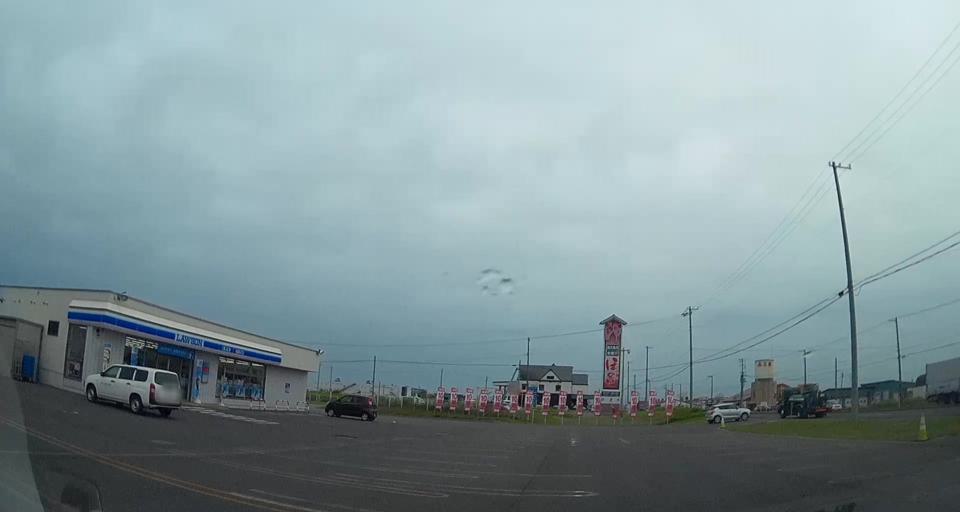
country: JP
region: Hokkaido
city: Tomakomai
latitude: 42.6154
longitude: 141.5299
